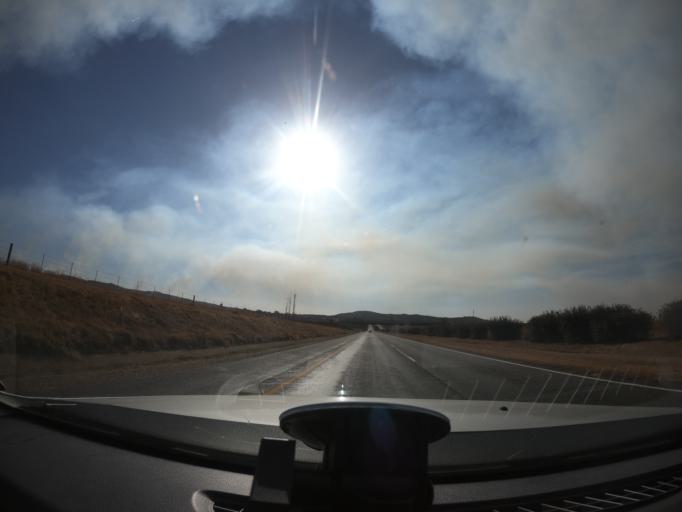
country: ZA
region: Gauteng
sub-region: Sedibeng District Municipality
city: Heidelberg
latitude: -26.5055
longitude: 28.3839
